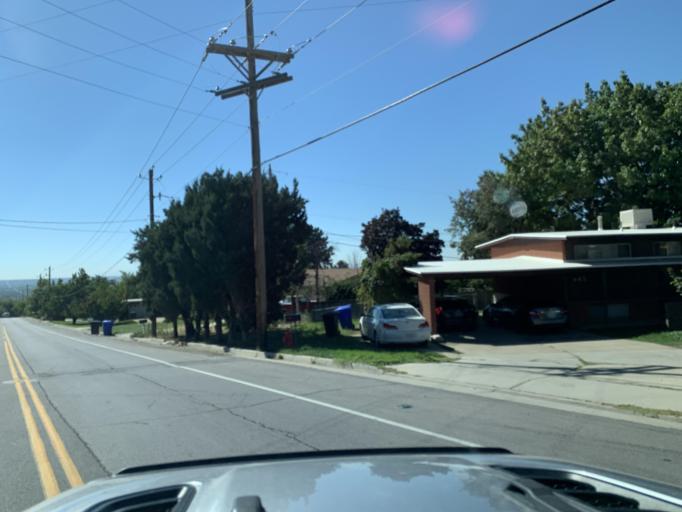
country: US
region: Utah
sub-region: Weber County
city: North Ogden
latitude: 41.3173
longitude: -111.9668
